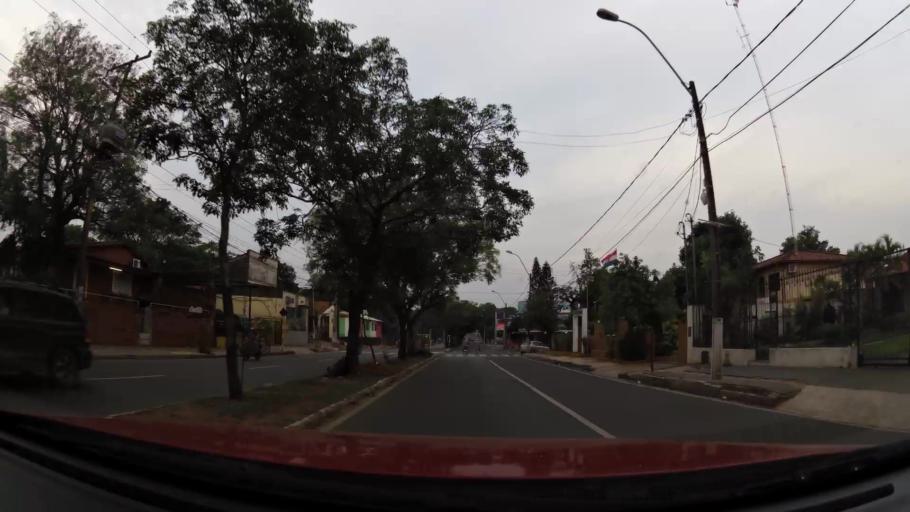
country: PY
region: Asuncion
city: Asuncion
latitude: -25.3201
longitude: -57.6217
